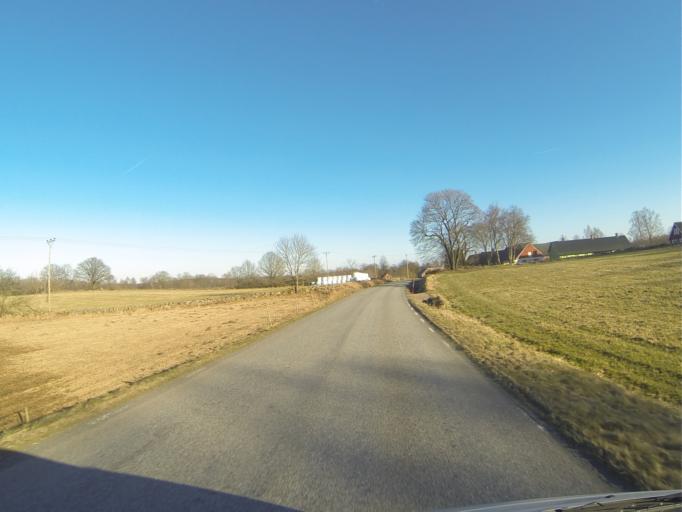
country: SE
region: Skane
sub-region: Horby Kommun
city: Hoerby
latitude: 55.9421
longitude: 13.6451
